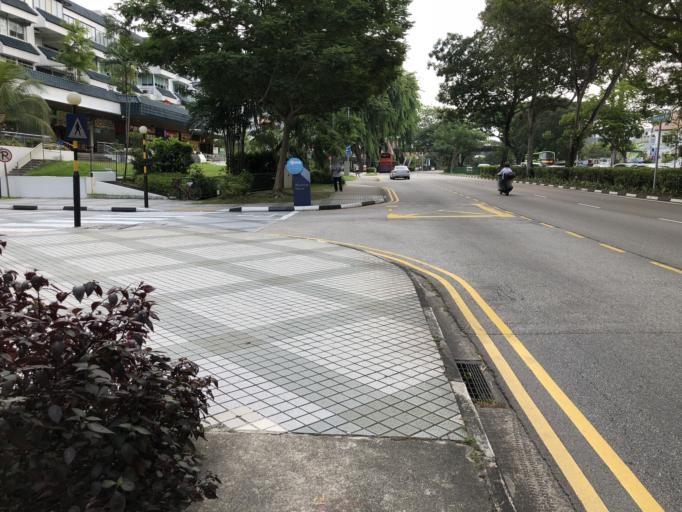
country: SG
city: Singapore
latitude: 1.3201
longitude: 103.8426
